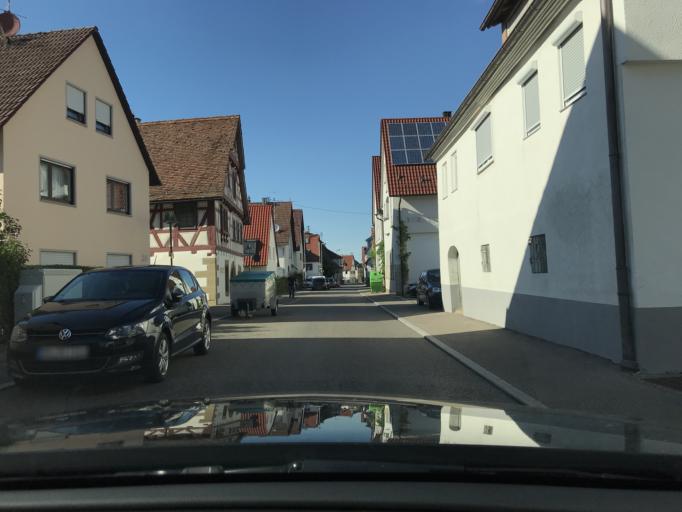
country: DE
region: Baden-Wuerttemberg
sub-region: Regierungsbezirk Stuttgart
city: Weinstadt-Endersbach
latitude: 48.7861
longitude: 9.3416
